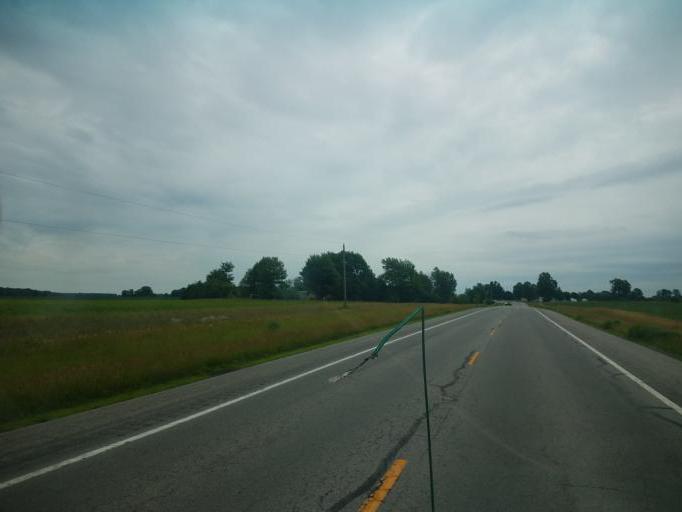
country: US
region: Ohio
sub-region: Hardin County
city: Ada
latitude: 40.7216
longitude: -83.7749
